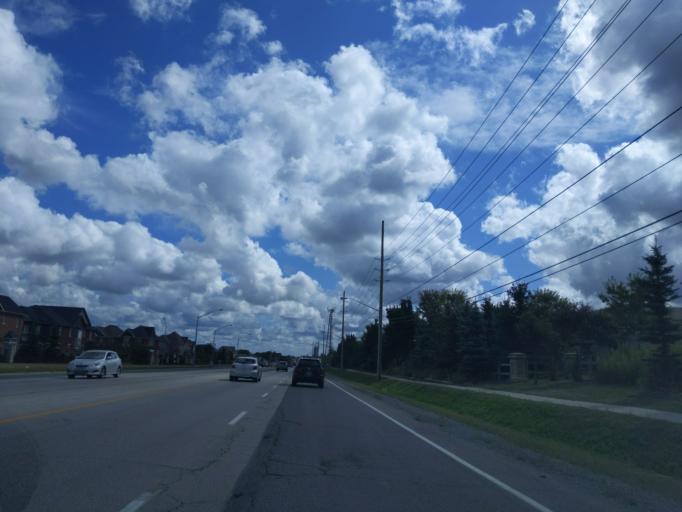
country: CA
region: Ontario
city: Vaughan
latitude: 43.8444
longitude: -79.4746
